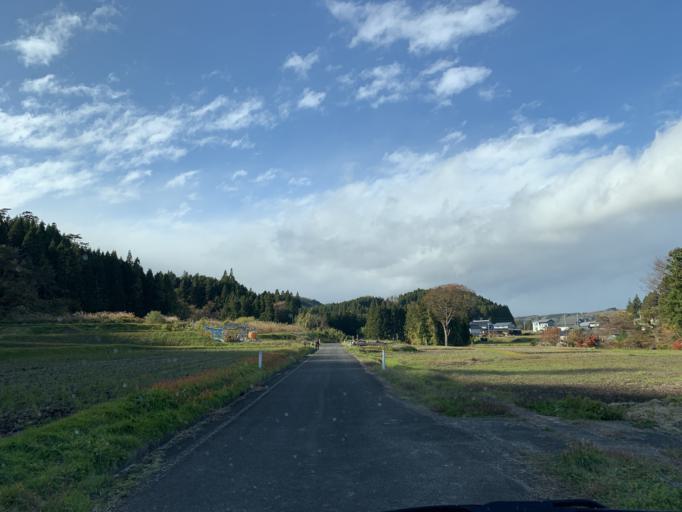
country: JP
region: Iwate
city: Ichinoseki
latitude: 39.0102
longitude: 141.0850
